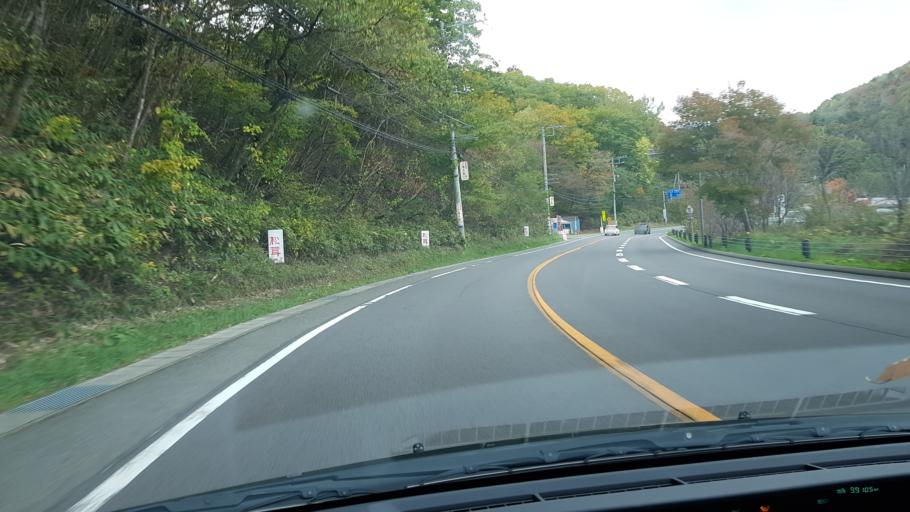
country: JP
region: Gunma
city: Nakanojomachi
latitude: 36.5979
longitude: 138.5872
